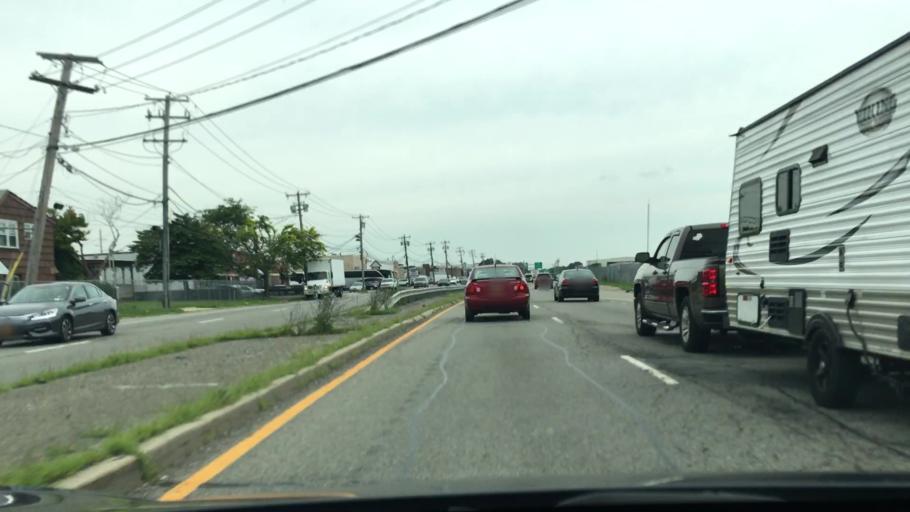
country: US
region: New York
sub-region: Suffolk County
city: East Farmingdale
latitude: 40.7187
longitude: -73.4105
